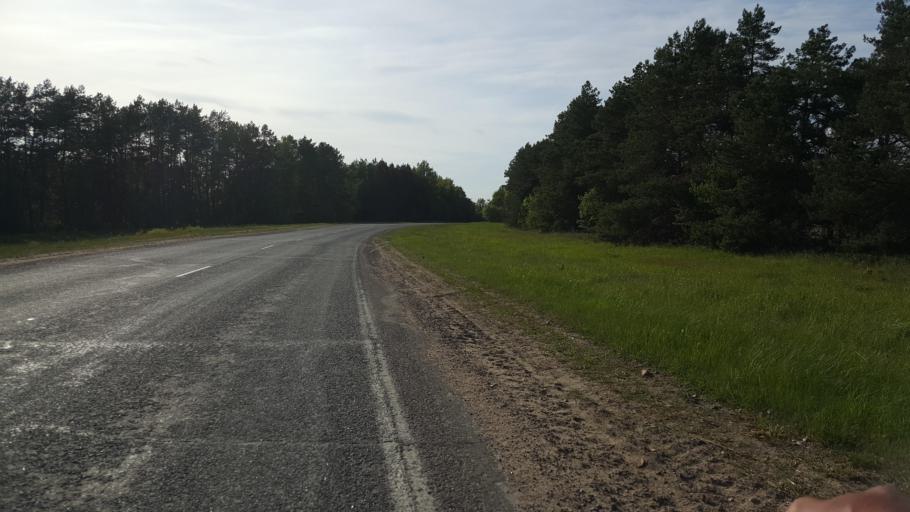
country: BY
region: Brest
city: Kamyanyets
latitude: 52.3863
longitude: 23.8492
